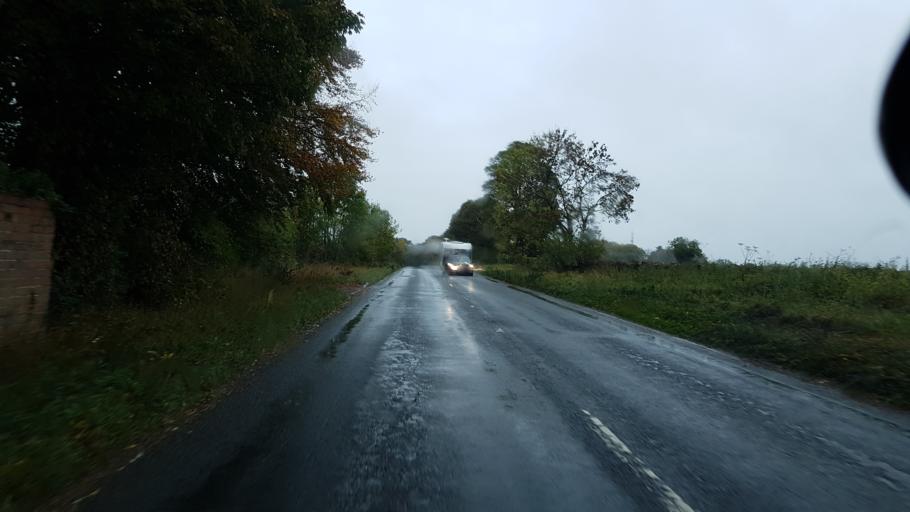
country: GB
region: England
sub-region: Gloucestershire
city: Stow on the Wold
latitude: 51.8947
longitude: -1.7104
